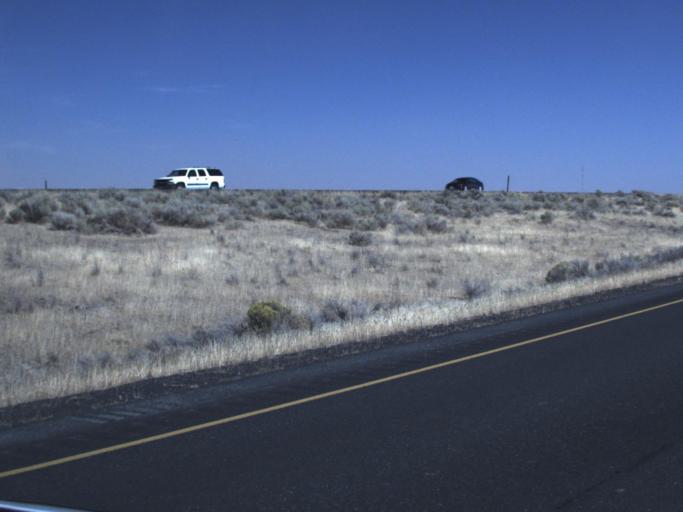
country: US
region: Washington
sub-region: Grant County
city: Warden
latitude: 47.0861
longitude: -118.7214
